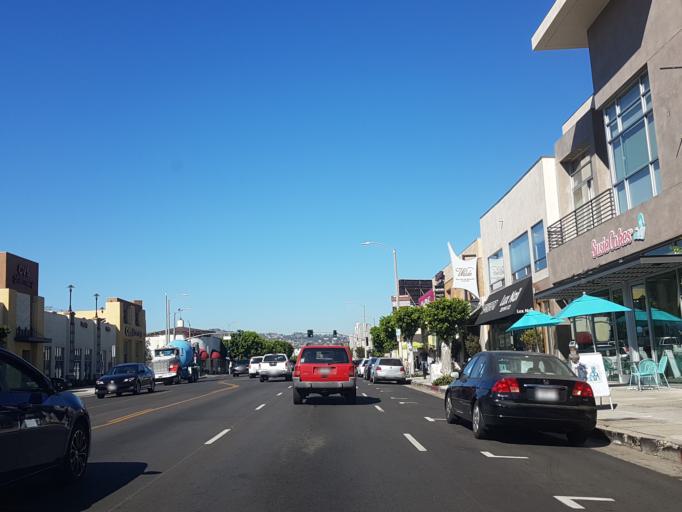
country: US
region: California
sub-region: Los Angeles County
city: West Hollywood
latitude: 34.0678
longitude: -118.3440
